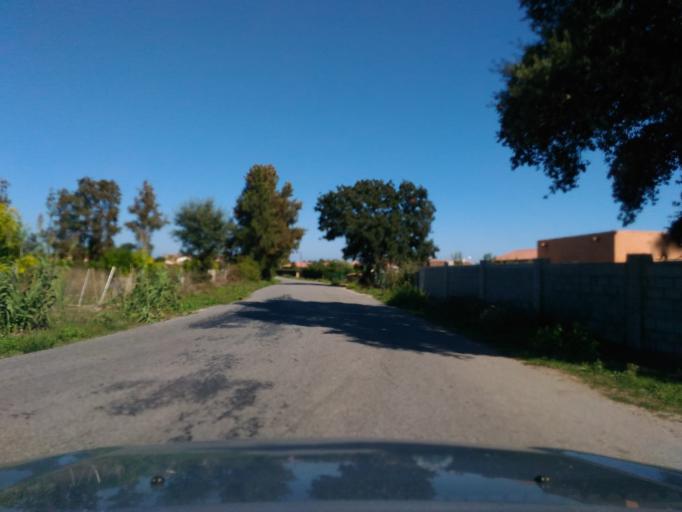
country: FR
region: Corsica
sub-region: Departement de la Haute-Corse
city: Aleria
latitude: 42.1108
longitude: 9.4797
